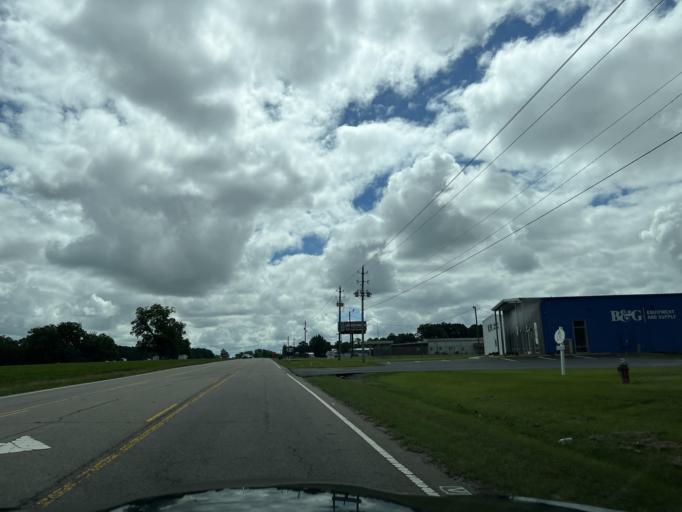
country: US
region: North Carolina
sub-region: Lee County
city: Sanford
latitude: 35.4379
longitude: -79.2042
